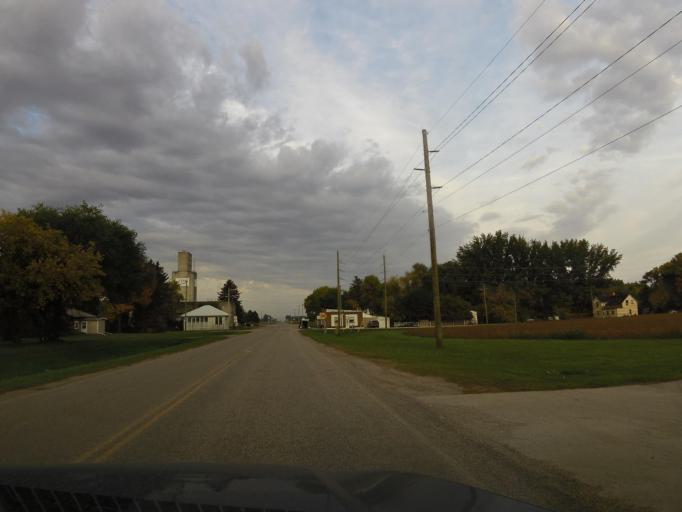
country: US
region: North Dakota
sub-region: Pembina County
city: Cavalier
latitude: 48.6882
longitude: -97.6649
